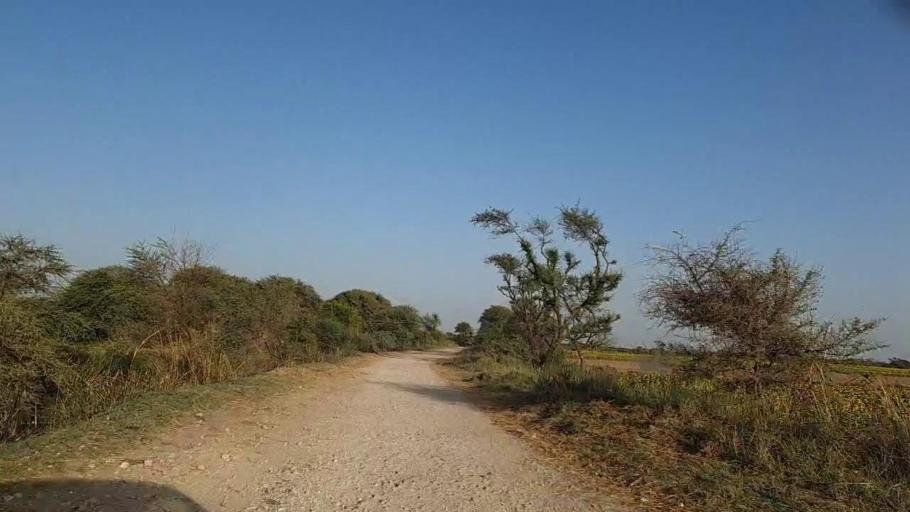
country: PK
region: Sindh
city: Jati
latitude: 24.4143
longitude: 68.3238
